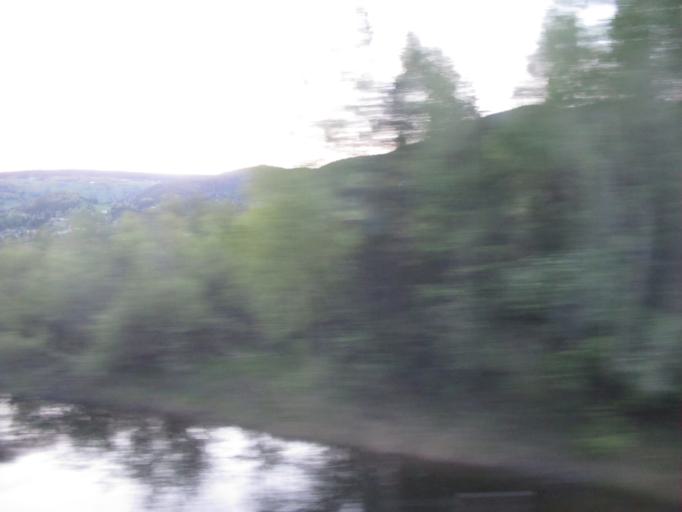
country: NO
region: Oppland
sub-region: Ringebu
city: Ringebu
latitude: 61.4447
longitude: 10.1879
